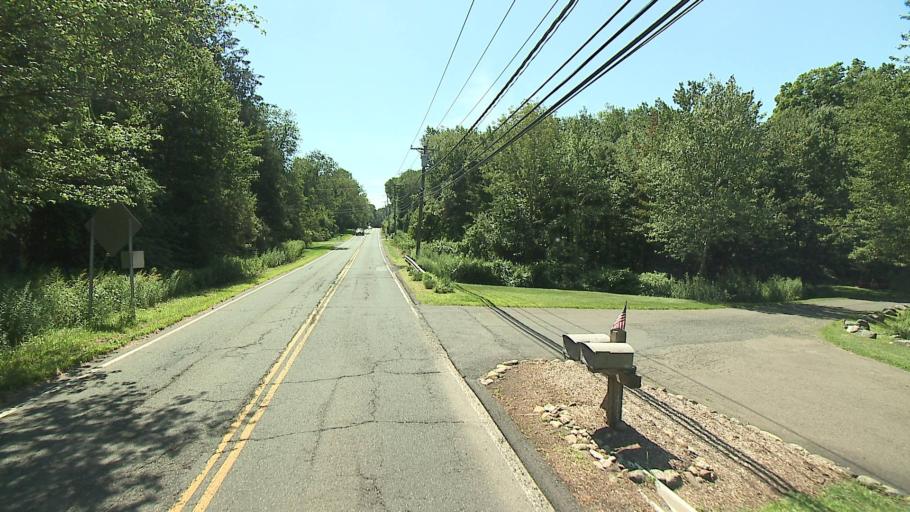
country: US
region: Connecticut
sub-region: New Haven County
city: Oxford
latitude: 41.3740
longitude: -73.1921
